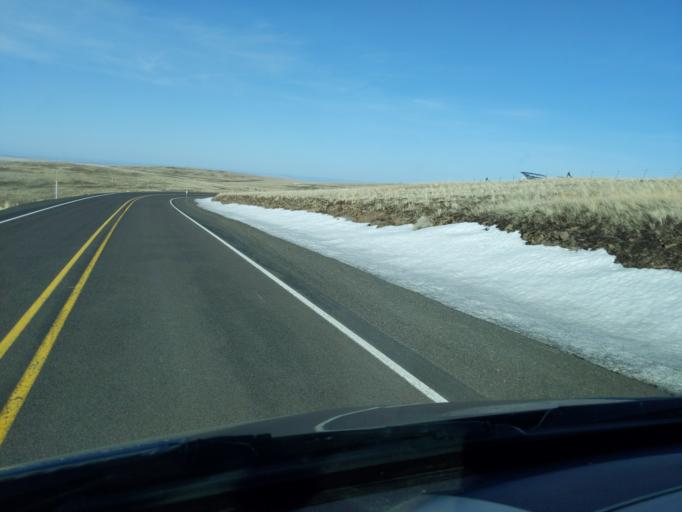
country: US
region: Oregon
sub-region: Umatilla County
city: Pilot Rock
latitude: 45.3029
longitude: -119.0050
